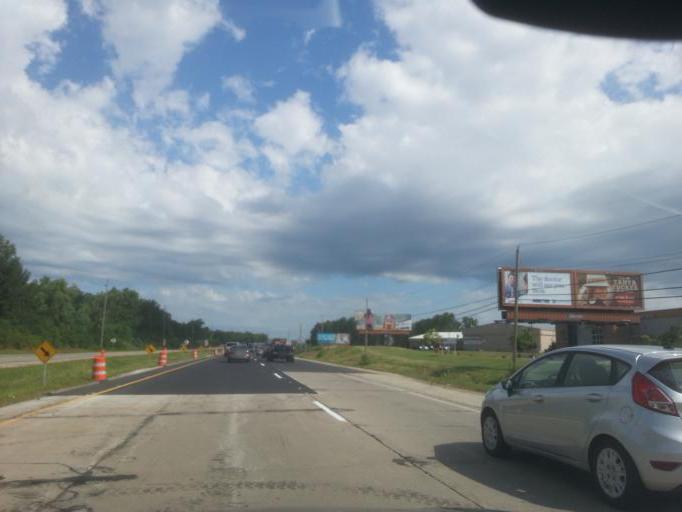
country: US
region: Wisconsin
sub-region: Dane County
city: Monona
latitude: 43.0527
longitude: -89.3084
